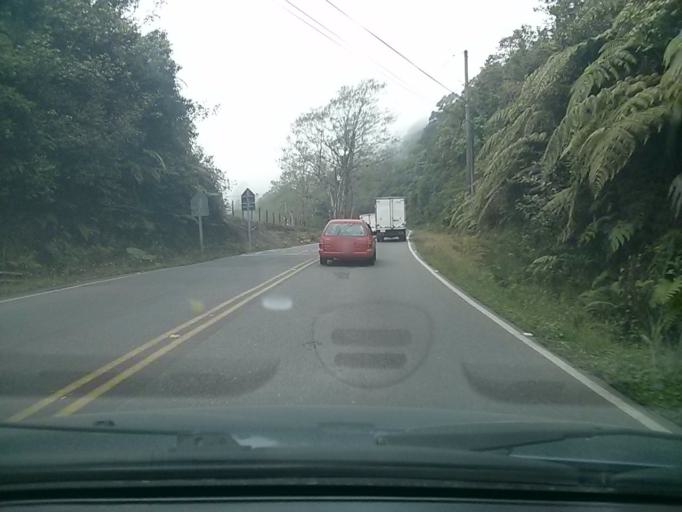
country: CR
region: Cartago
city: Tobosi
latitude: 9.7411
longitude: -83.9589
